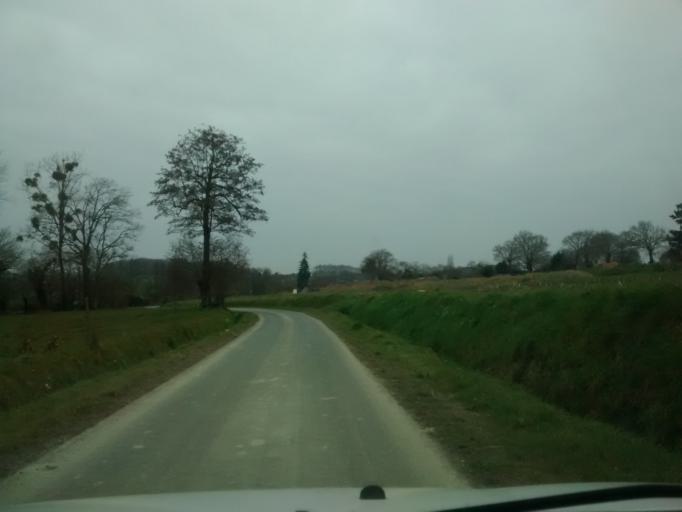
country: FR
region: Brittany
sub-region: Departement d'Ille-et-Vilaine
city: Bazouges-la-Perouse
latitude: 48.3861
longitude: -1.5559
